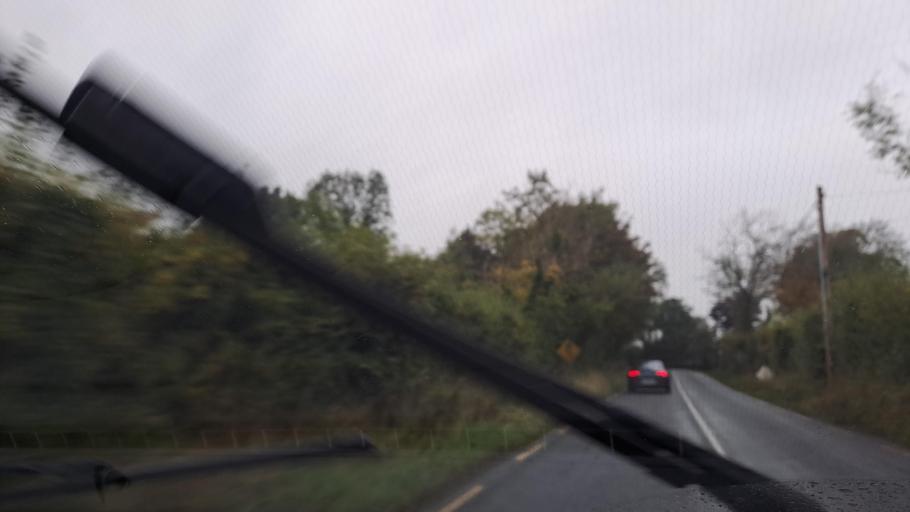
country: IE
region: Ulster
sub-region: County Monaghan
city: Monaghan
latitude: 54.2231
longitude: -6.9302
